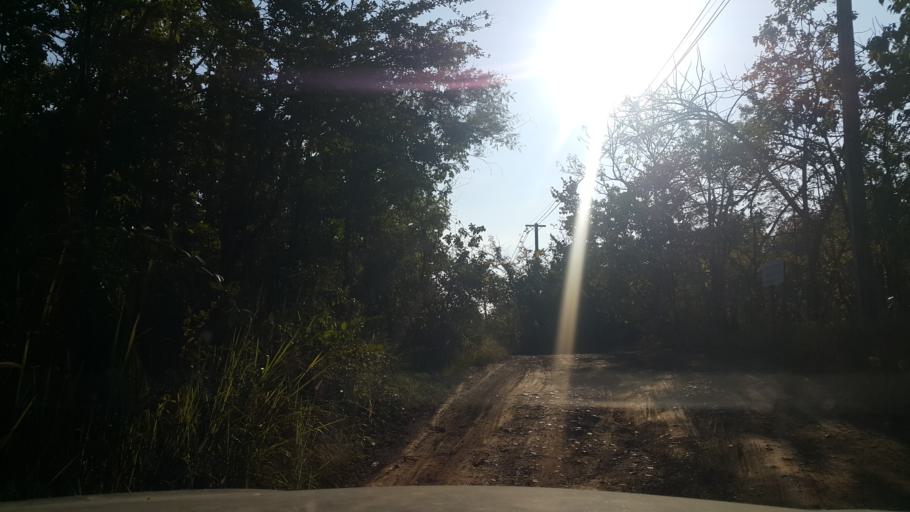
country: TH
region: Lamphun
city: Mae Tha
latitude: 18.5206
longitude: 99.1172
